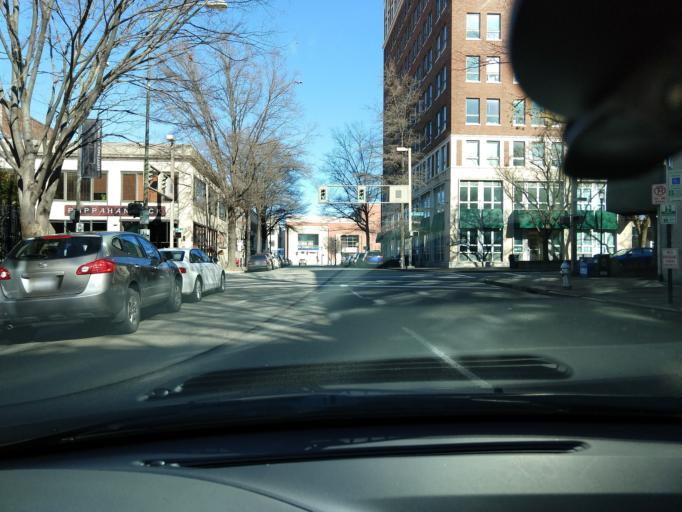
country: US
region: Virginia
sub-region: City of Richmond
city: Richmond
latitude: 37.5425
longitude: -77.4394
